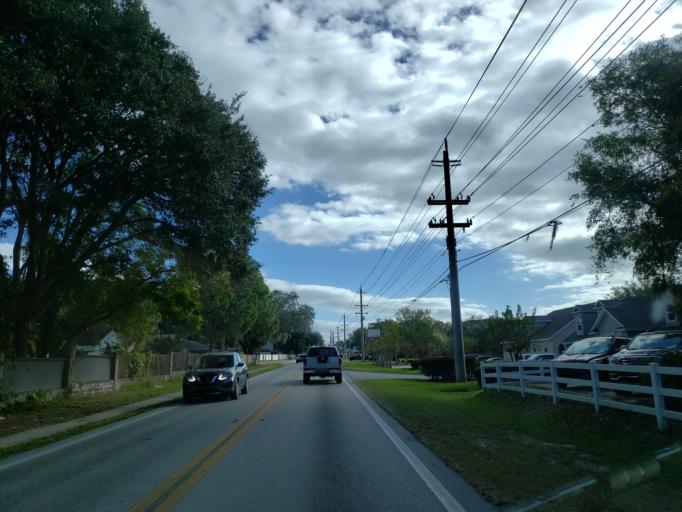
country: US
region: Florida
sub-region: Polk County
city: Medulla
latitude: 27.9749
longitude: -81.9649
